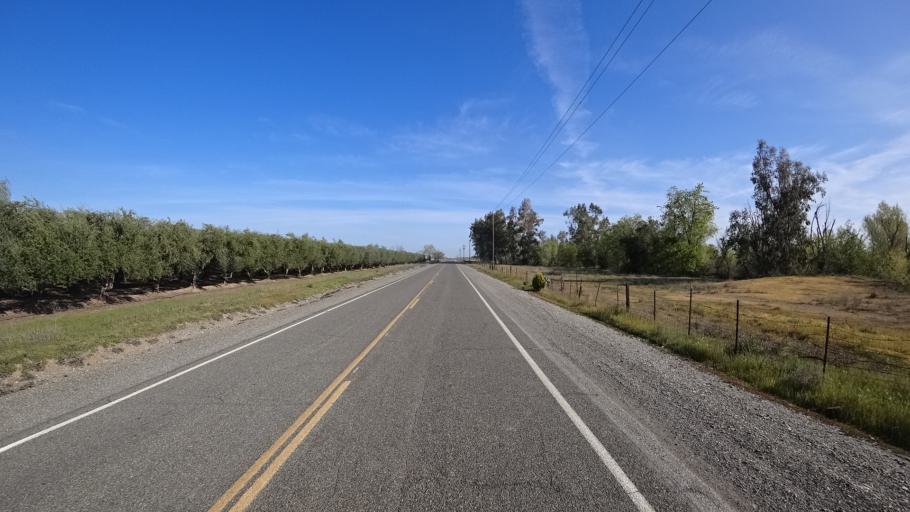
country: US
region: California
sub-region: Glenn County
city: Willows
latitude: 39.5438
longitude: -122.1650
